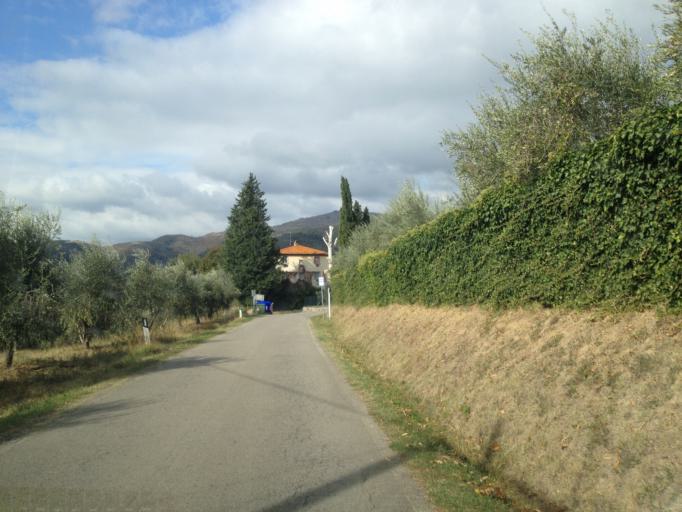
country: IT
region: Tuscany
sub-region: Province of Florence
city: Montebonello
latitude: 43.8582
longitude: 11.5054
